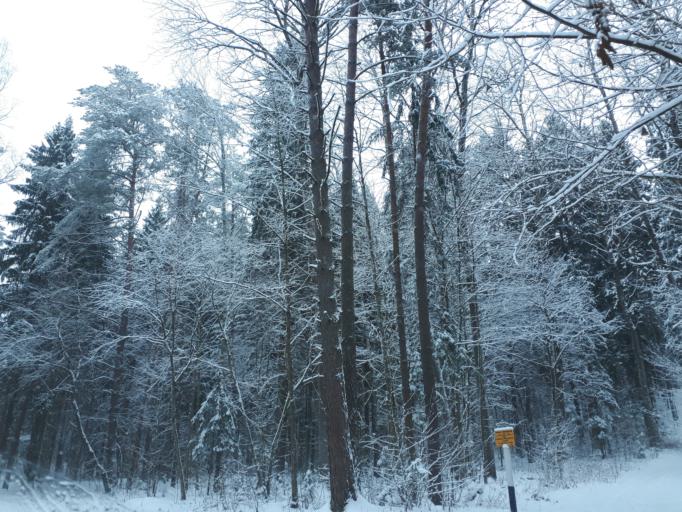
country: BY
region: Vitebsk
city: Vitebsk
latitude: 55.2629
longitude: 30.2127
